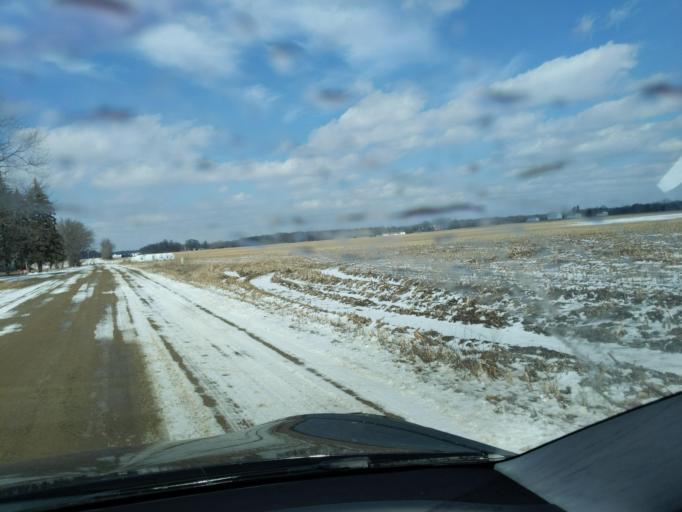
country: US
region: Michigan
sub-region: Livingston County
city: Fowlerville
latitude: 42.6280
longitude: -84.0620
